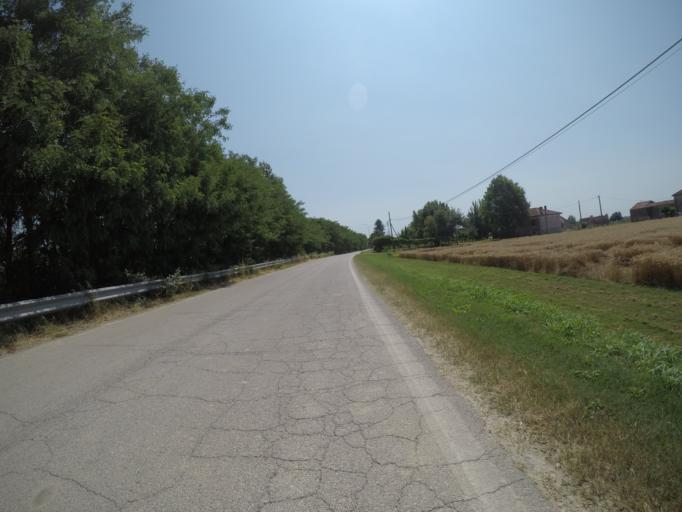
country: IT
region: Veneto
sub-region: Provincia di Rovigo
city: Pincara
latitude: 45.0021
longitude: 11.6372
